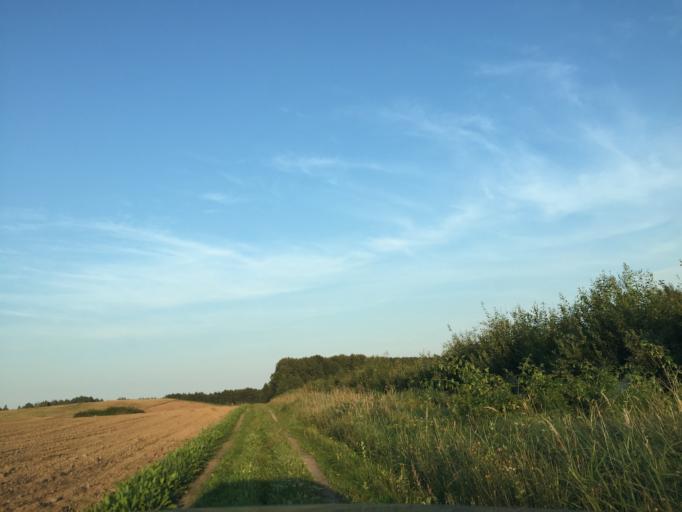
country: LV
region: Limbazu Rajons
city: Limbazi
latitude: 57.5751
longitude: 24.7739
